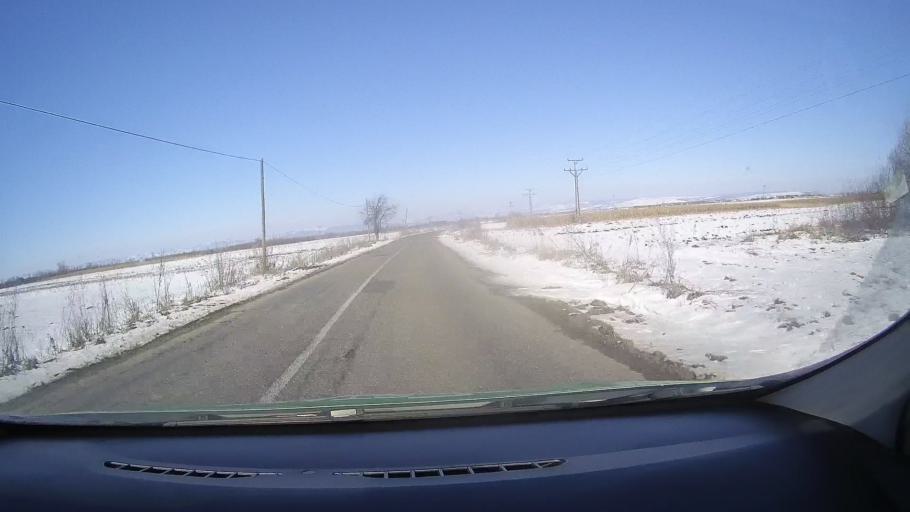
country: RO
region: Brasov
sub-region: Comuna Harseni
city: Harseni
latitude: 45.7658
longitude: 25.0044
